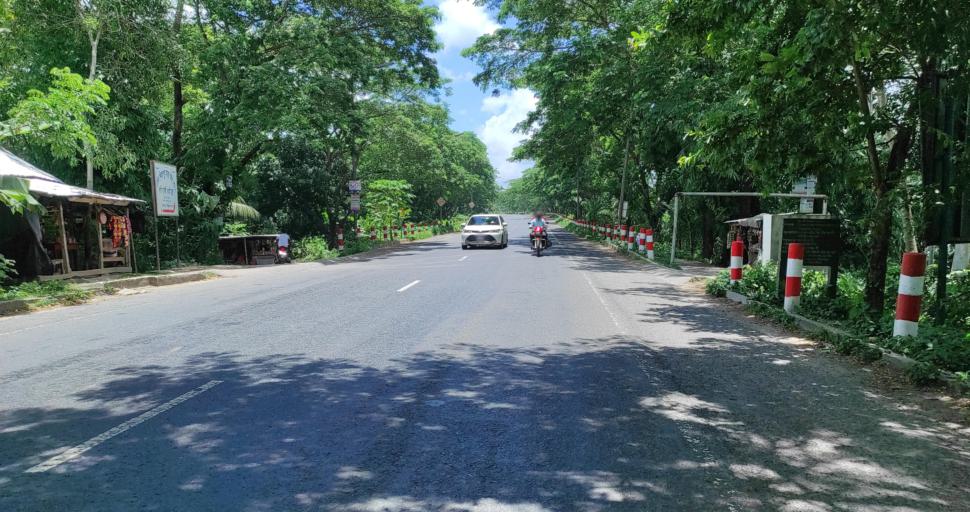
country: BD
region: Barisal
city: Gaurnadi
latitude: 22.8273
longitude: 90.2598
